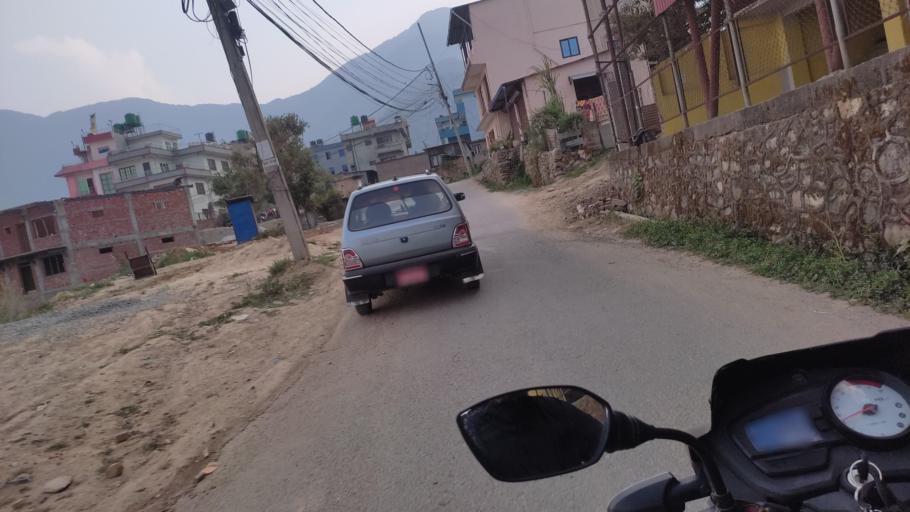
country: NP
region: Central Region
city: Kirtipur
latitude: 27.6767
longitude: 85.2537
